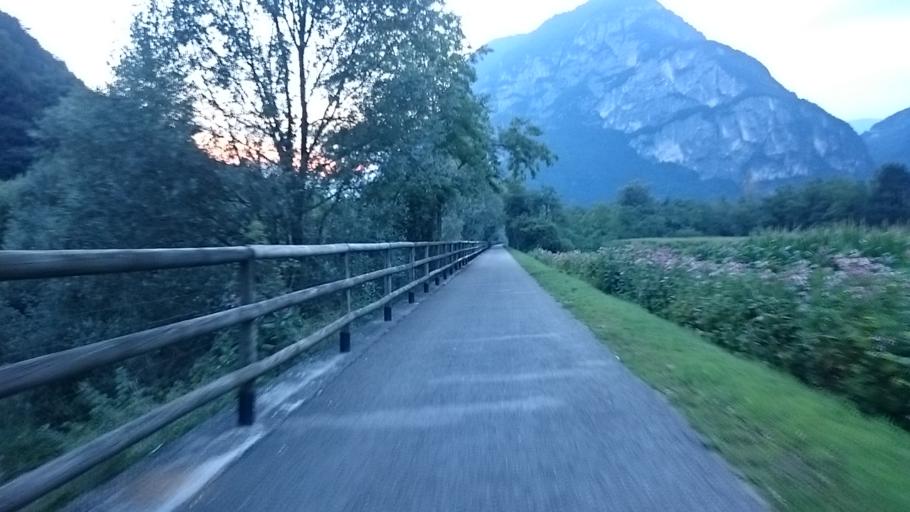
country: IT
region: Trentino-Alto Adige
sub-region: Provincia di Trento
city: Grigno
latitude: 46.0052
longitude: 11.6435
